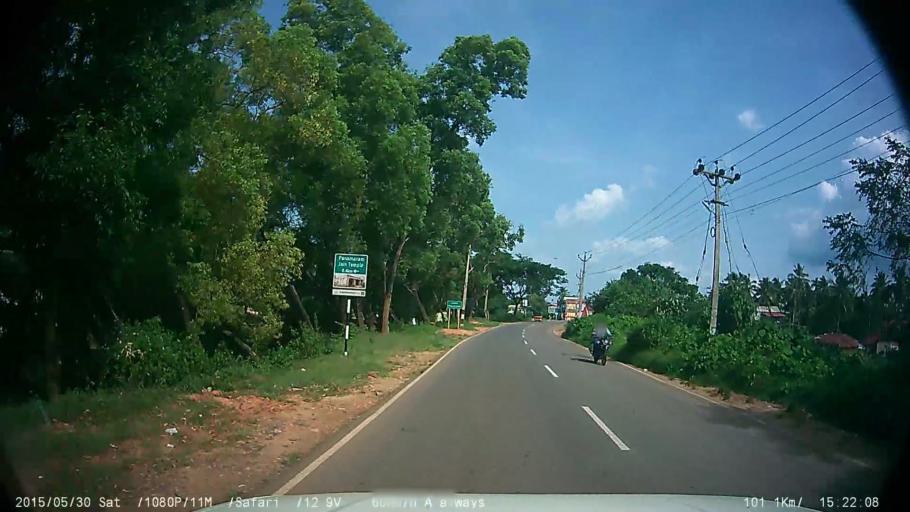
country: IN
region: Kerala
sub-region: Wayanad
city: Panamaram
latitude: 11.7433
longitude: 76.0721
